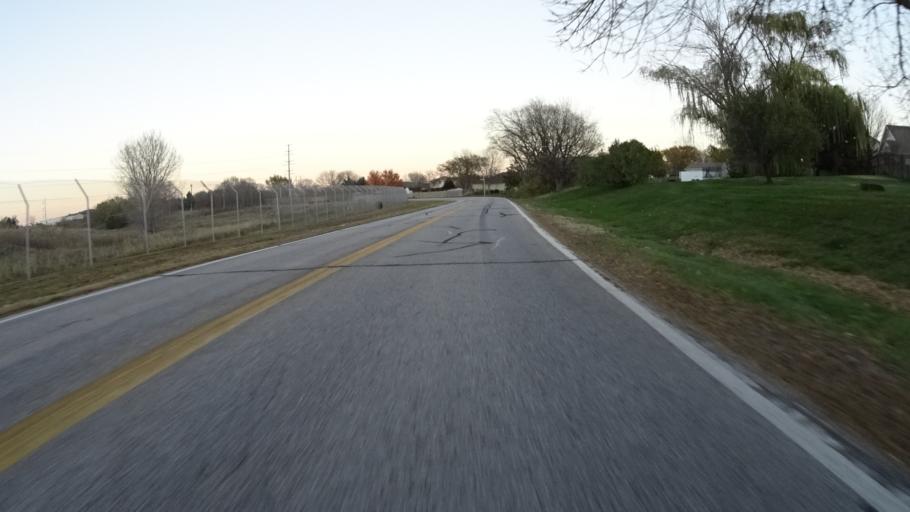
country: US
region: Nebraska
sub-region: Sarpy County
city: Offutt Air Force Base
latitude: 41.1675
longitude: -95.9552
